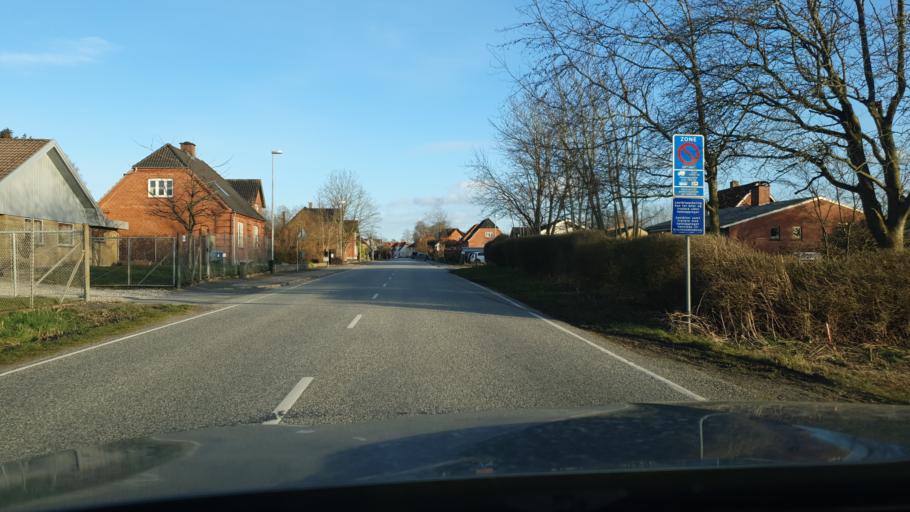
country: DK
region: Zealand
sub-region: Naestved Kommune
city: Fuglebjerg
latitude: 55.3093
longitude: 11.5432
